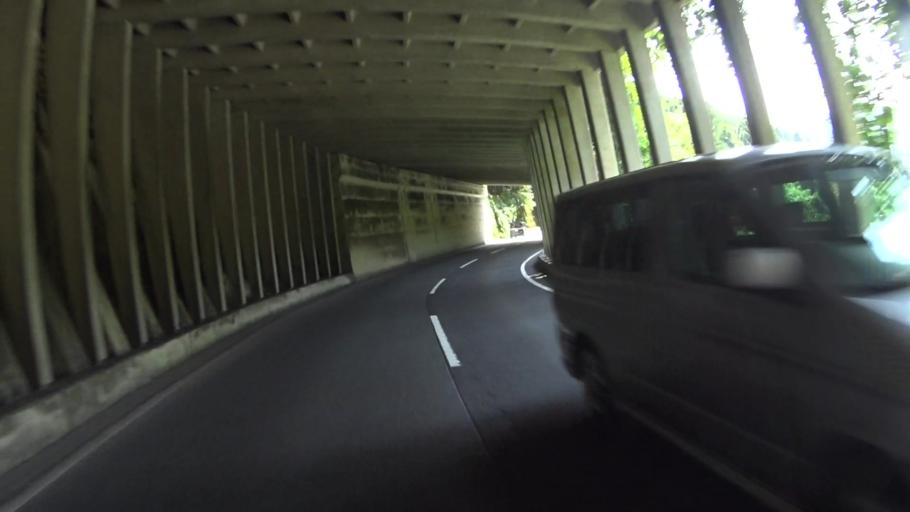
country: JP
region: Fukui
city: Obama
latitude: 35.4297
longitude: 135.6939
